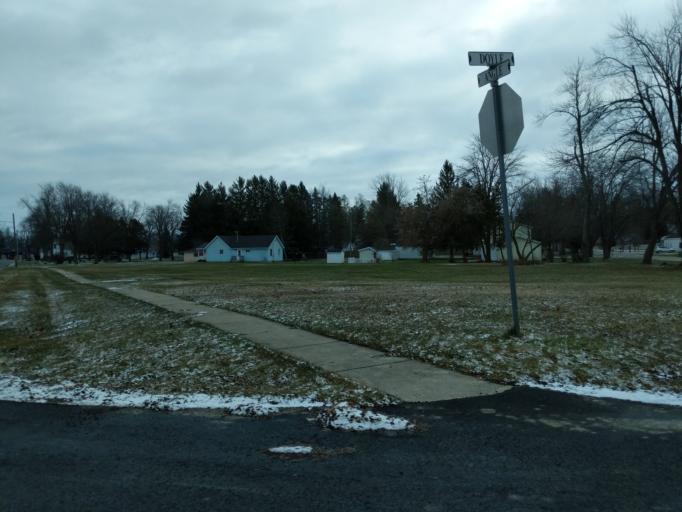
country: US
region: Michigan
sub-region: Sanilac County
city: Marlette
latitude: 43.3319
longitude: -83.0825
